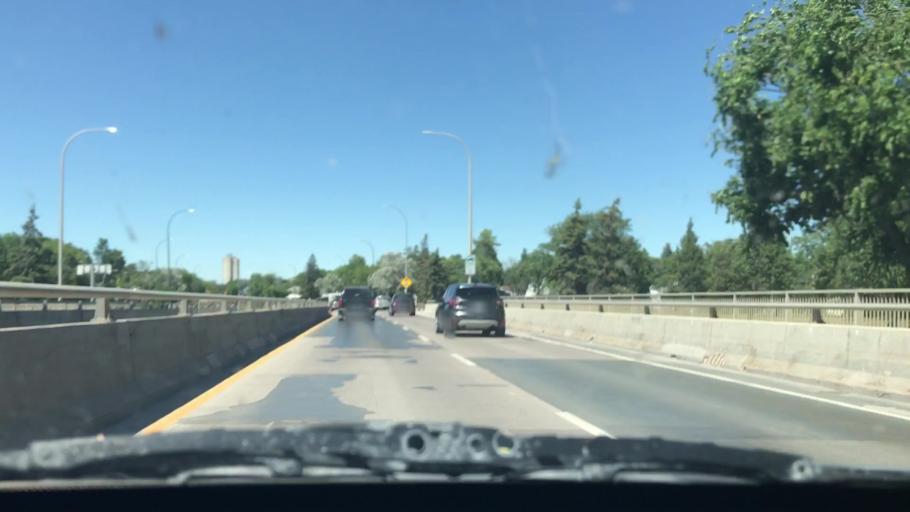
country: CA
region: Manitoba
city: Winnipeg
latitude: 49.8564
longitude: -97.1272
